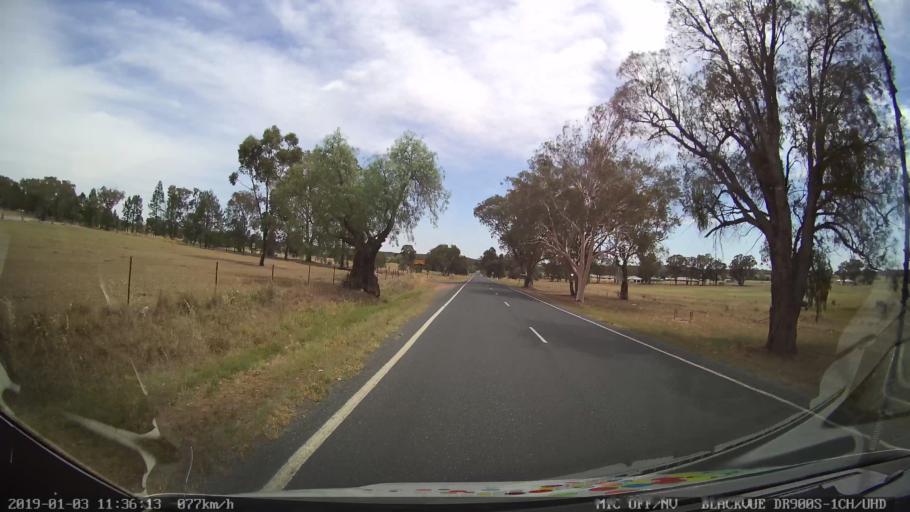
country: AU
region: New South Wales
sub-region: Weddin
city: Grenfell
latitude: -33.9133
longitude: 148.1595
